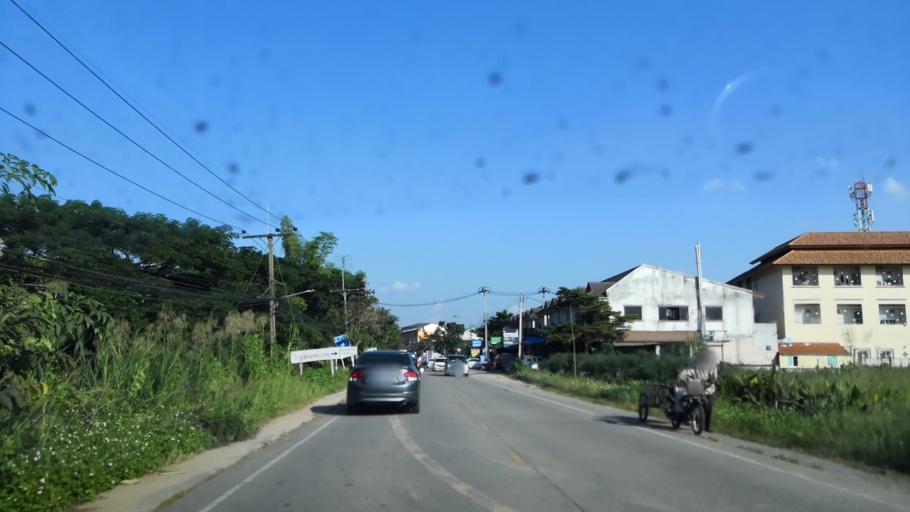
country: TH
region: Chiang Rai
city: Chiang Rai
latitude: 19.9296
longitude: 99.8598
